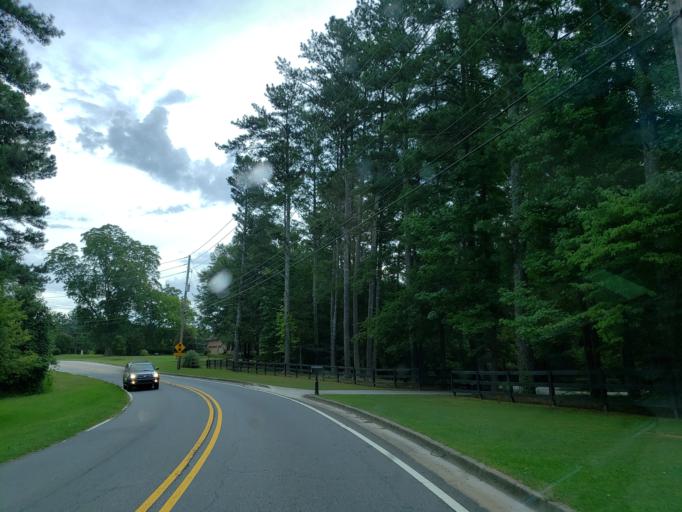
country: US
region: Georgia
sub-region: Cobb County
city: Acworth
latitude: 34.0195
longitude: -84.7021
